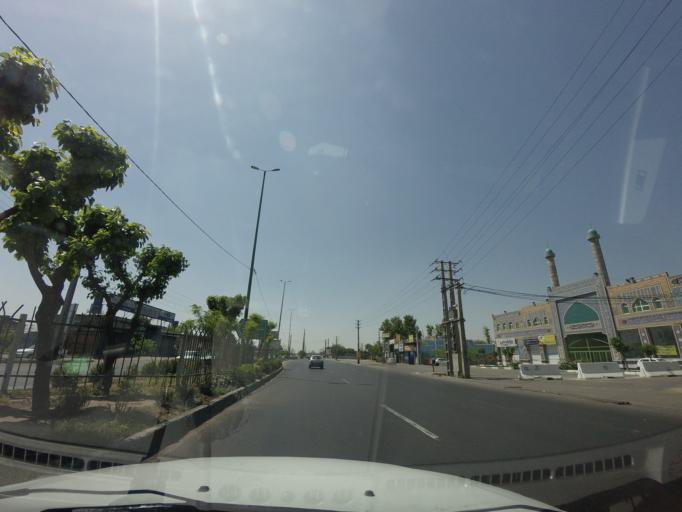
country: IR
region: Tehran
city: Eslamshahr
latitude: 35.6001
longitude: 51.2995
